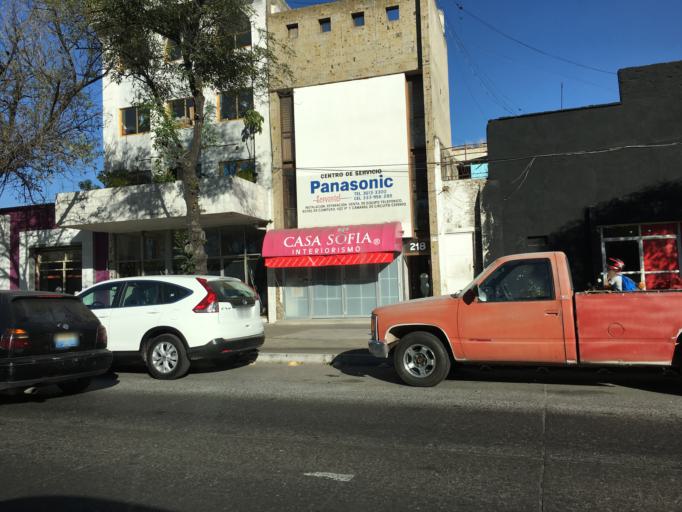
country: MX
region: Jalisco
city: Guadalajara
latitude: 20.6797
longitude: -103.3541
